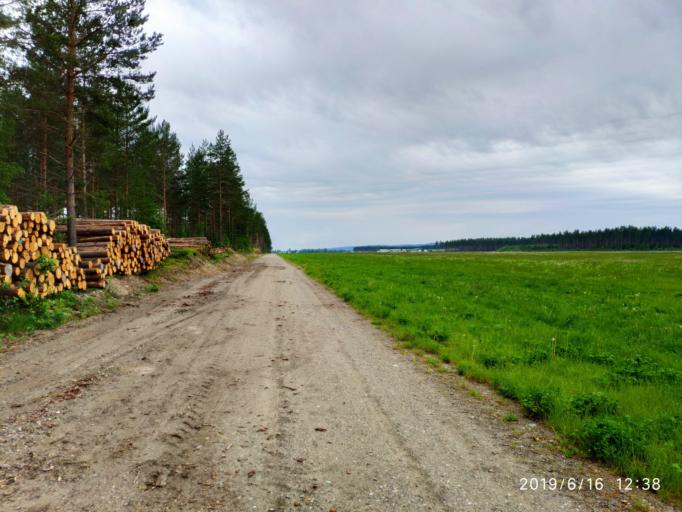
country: NO
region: Oppland
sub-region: Jevnaker
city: Jevnaker
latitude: 60.2199
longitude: 10.3320
